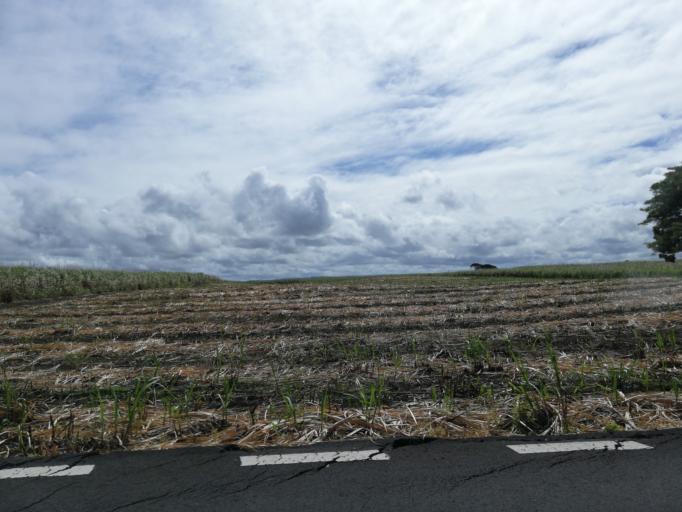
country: MU
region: Grand Port
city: Plaine Magnien
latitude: -20.4530
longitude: 57.6751
